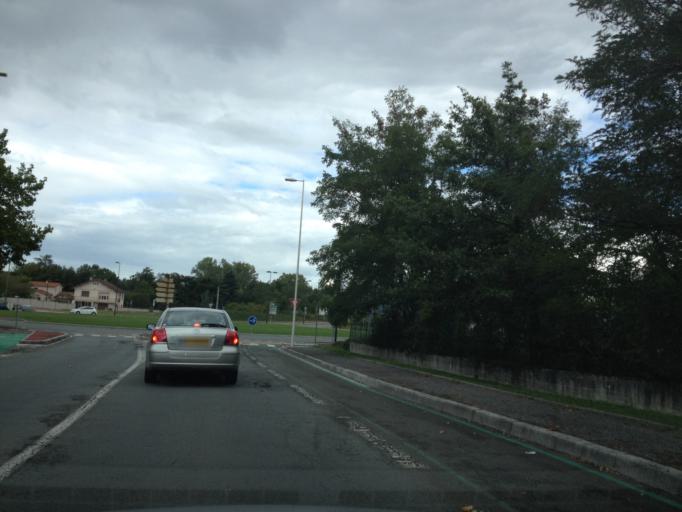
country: FR
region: Rhone-Alpes
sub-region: Departement de la Loire
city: Riorges
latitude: 46.0304
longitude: 4.0470
